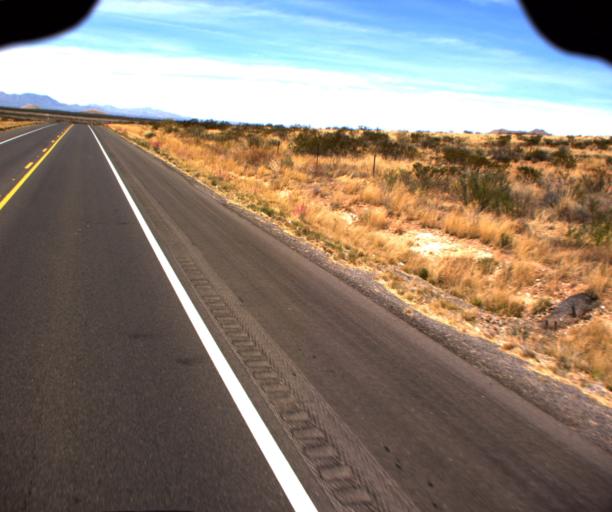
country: US
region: Arizona
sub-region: Cochise County
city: Willcox
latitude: 31.9017
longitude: -109.7112
